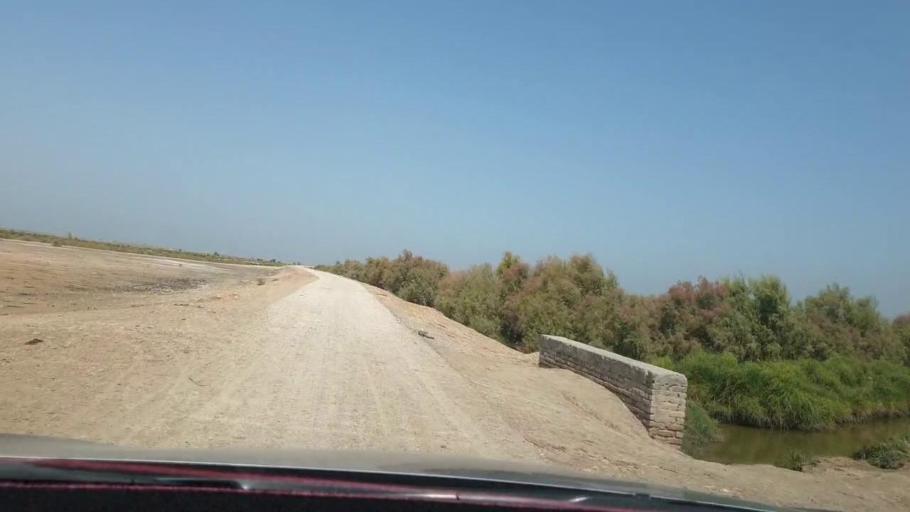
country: PK
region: Sindh
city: Warah
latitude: 27.5261
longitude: 67.7108
